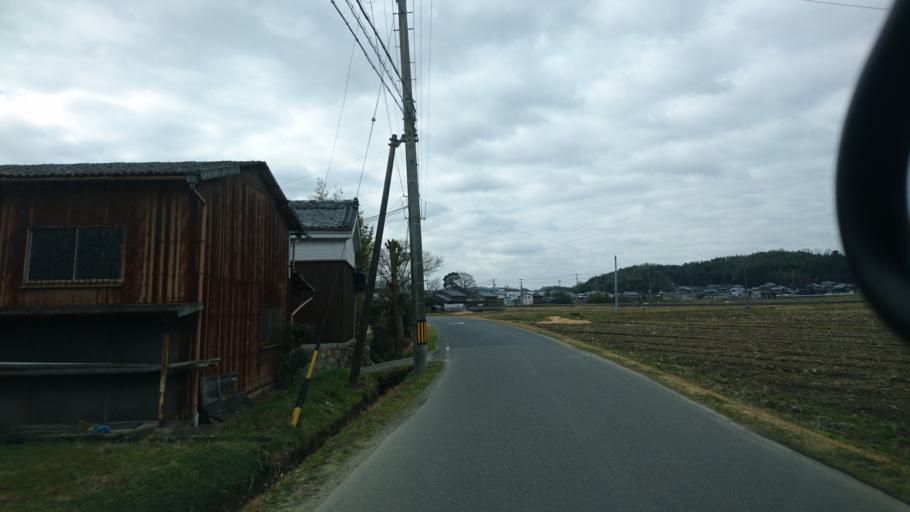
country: JP
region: Mie
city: Ueno-ebisumachi
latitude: 34.7446
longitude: 136.1114
